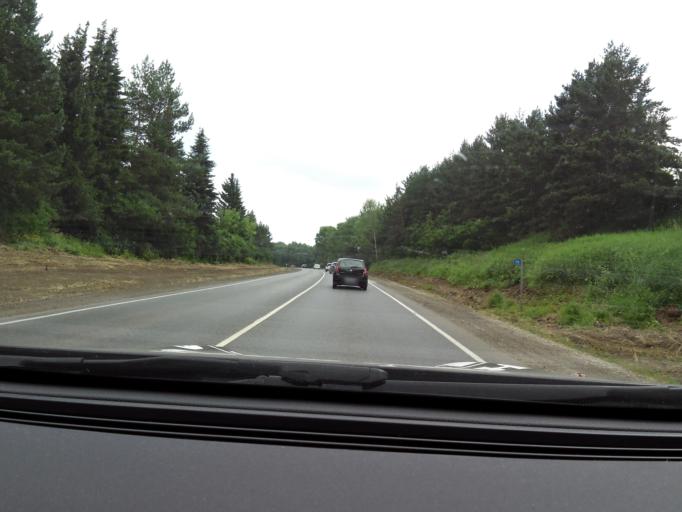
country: RU
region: Perm
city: Kungur
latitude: 57.4535
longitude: 56.7716
